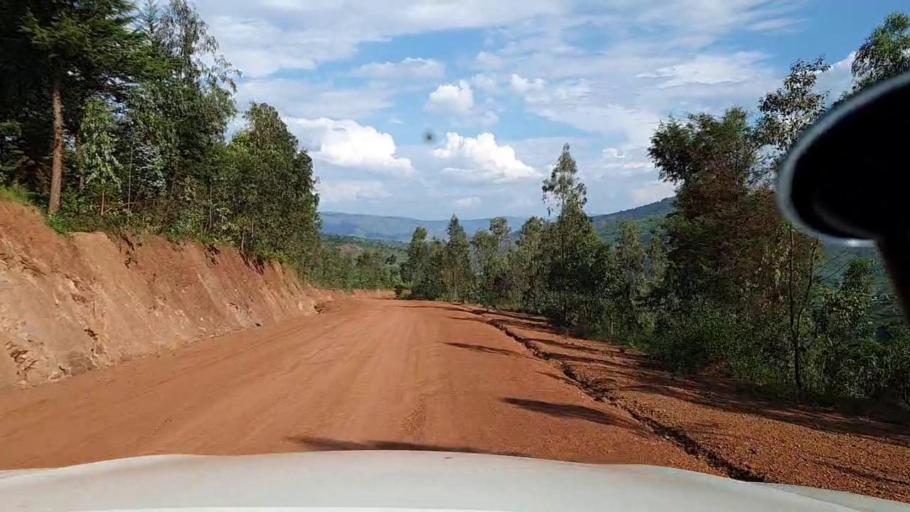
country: RW
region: Kigali
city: Kigali
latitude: -1.8435
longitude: 29.8586
